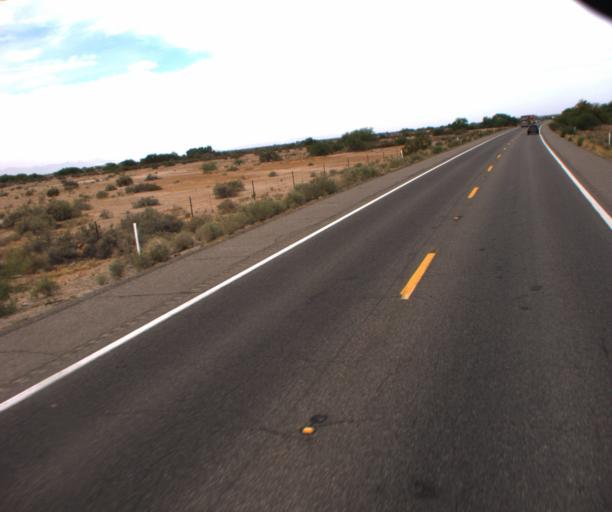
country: US
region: Arizona
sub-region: Pinal County
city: Sacaton
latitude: 33.0742
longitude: -111.7013
